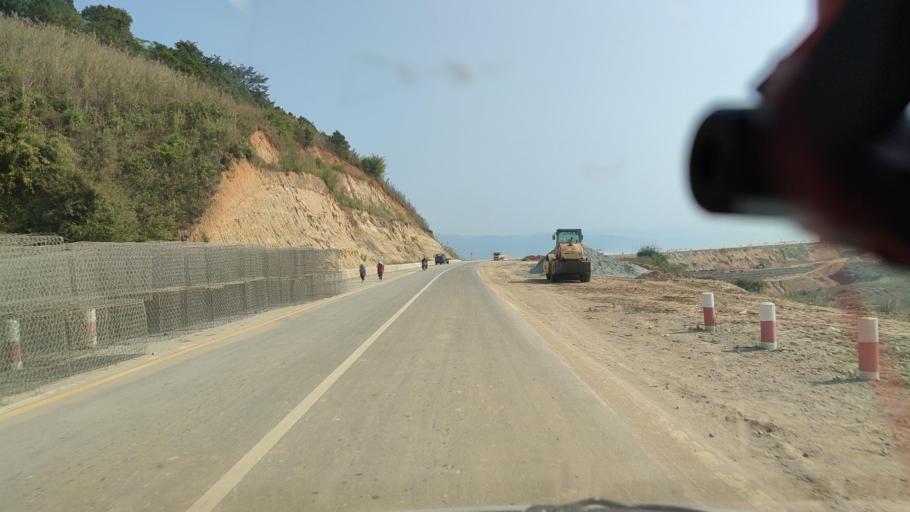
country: TH
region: Chiang Rai
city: Mae Sai
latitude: 21.2708
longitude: 99.5888
